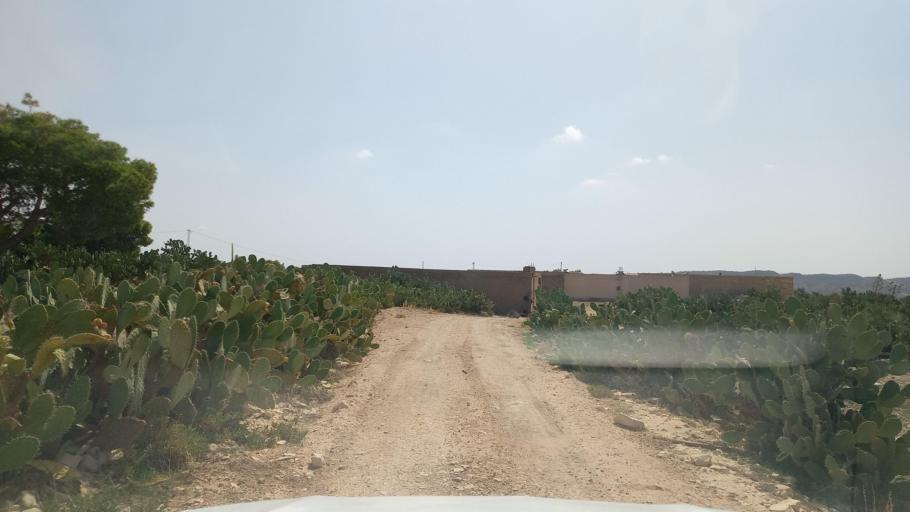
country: TN
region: Al Qasrayn
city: Sbiba
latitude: 35.4054
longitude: 8.9713
